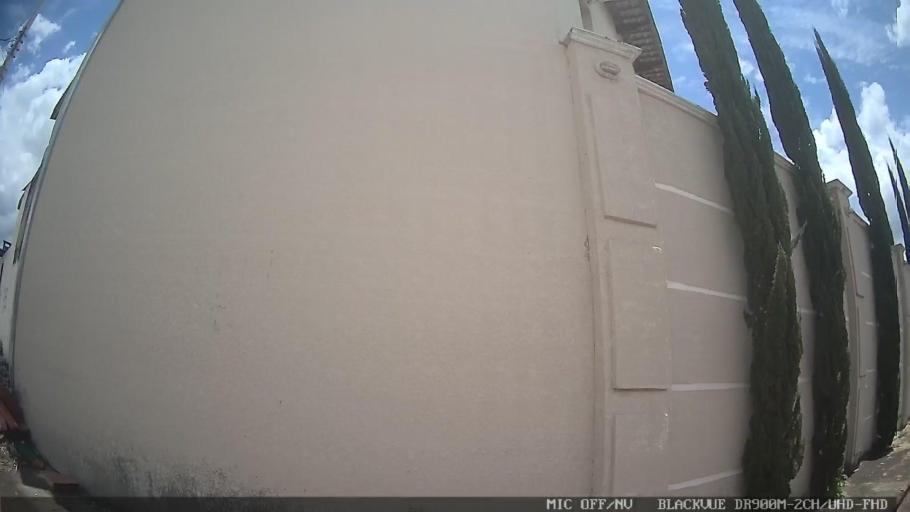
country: BR
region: Sao Paulo
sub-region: Atibaia
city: Atibaia
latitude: -23.1046
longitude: -46.5453
